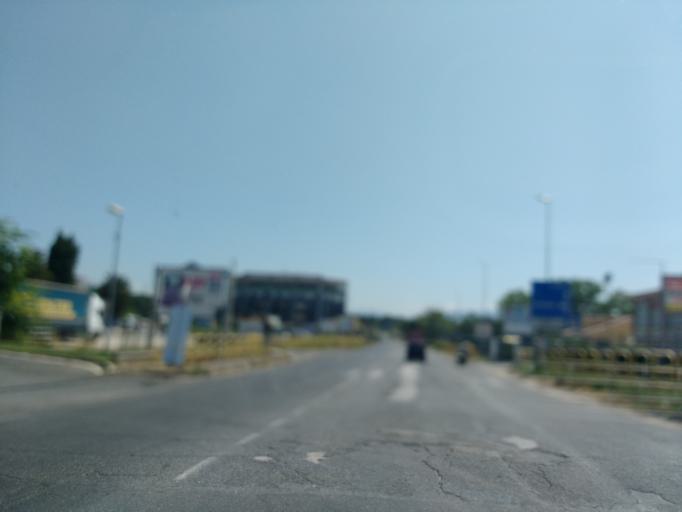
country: IT
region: Latium
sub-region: Citta metropolitana di Roma Capitale
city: Albuccione
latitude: 41.9519
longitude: 12.6903
